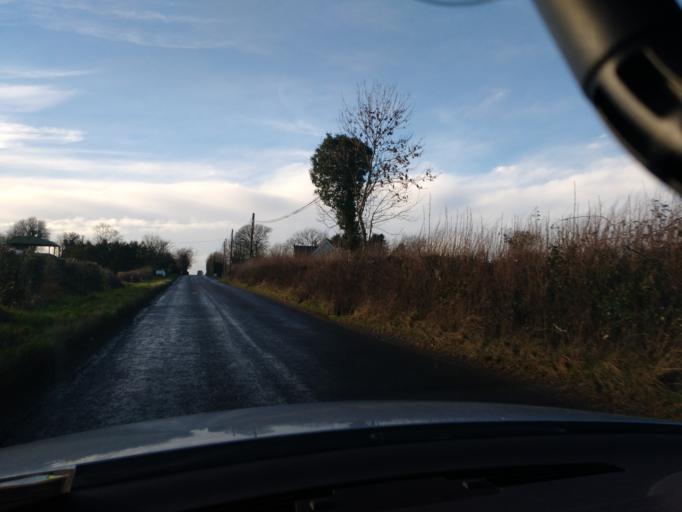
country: IE
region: Munster
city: Thurles
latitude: 52.6323
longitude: -7.7587
